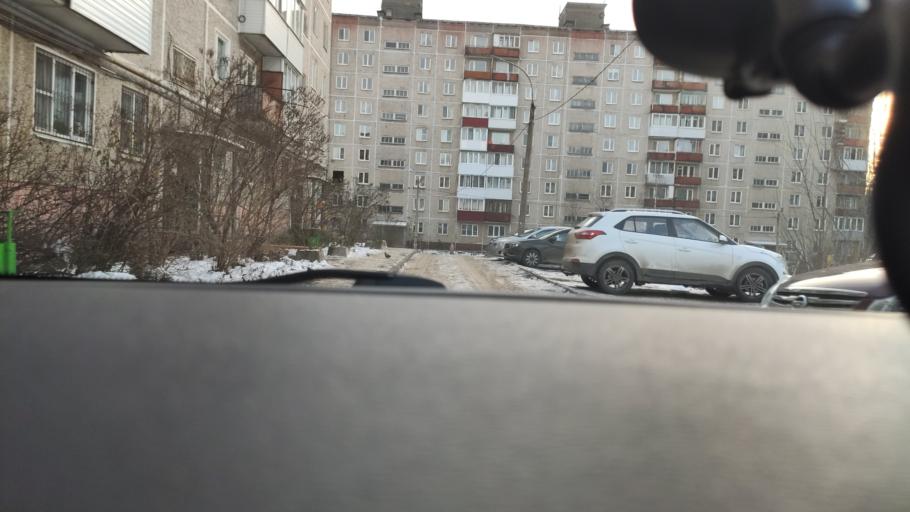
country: RU
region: Perm
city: Perm
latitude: 58.1105
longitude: 56.2831
